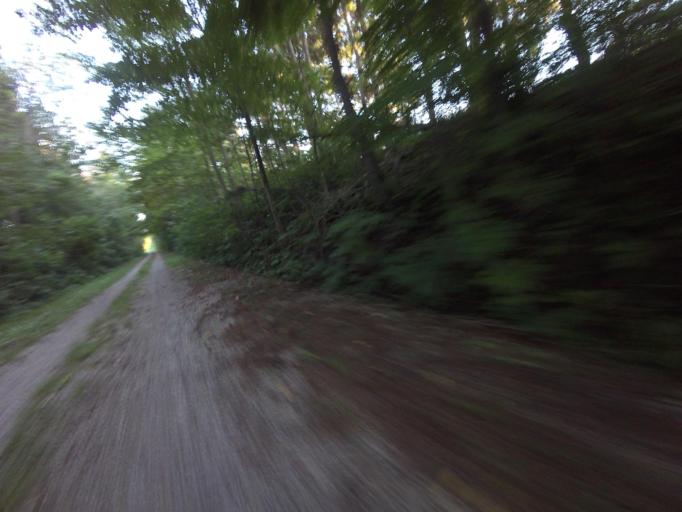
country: CA
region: Ontario
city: Goderich
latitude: 43.7504
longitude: -81.6582
